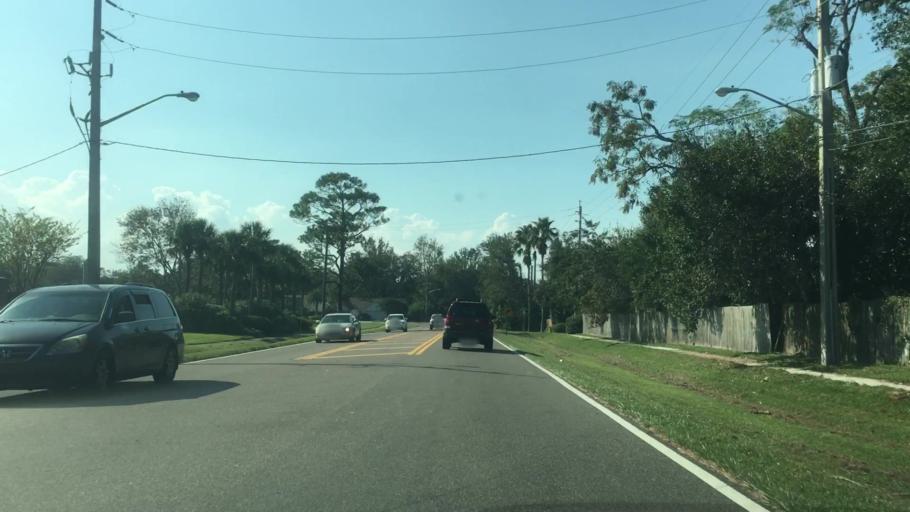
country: US
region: Florida
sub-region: Duval County
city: Neptune Beach
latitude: 30.3008
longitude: -81.4409
